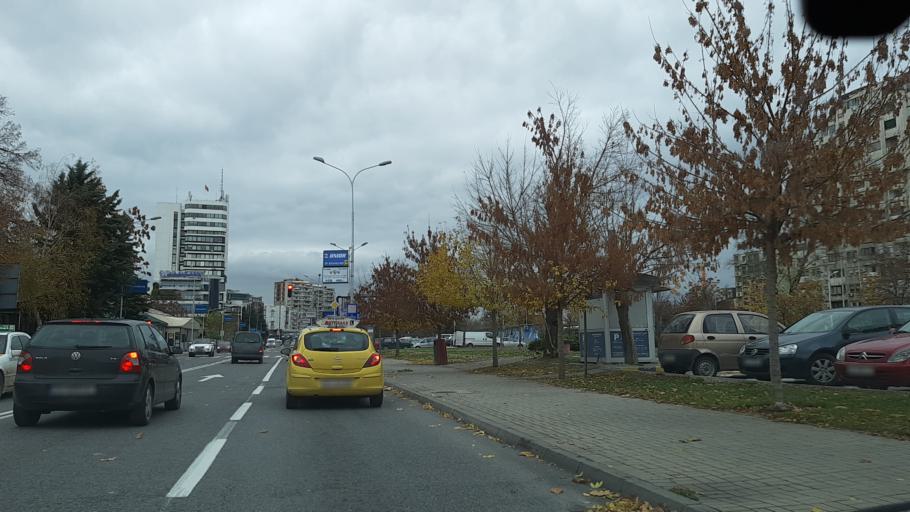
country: MK
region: Karpos
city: Skopje
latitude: 41.9940
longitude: 21.4204
